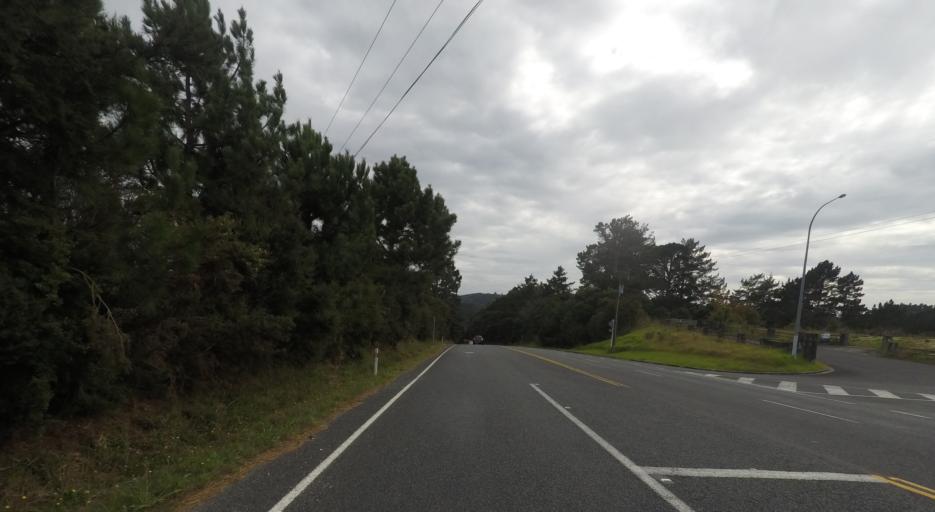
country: NZ
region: Auckland
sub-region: Auckland
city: Rothesay Bay
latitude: -36.6889
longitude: 174.7058
